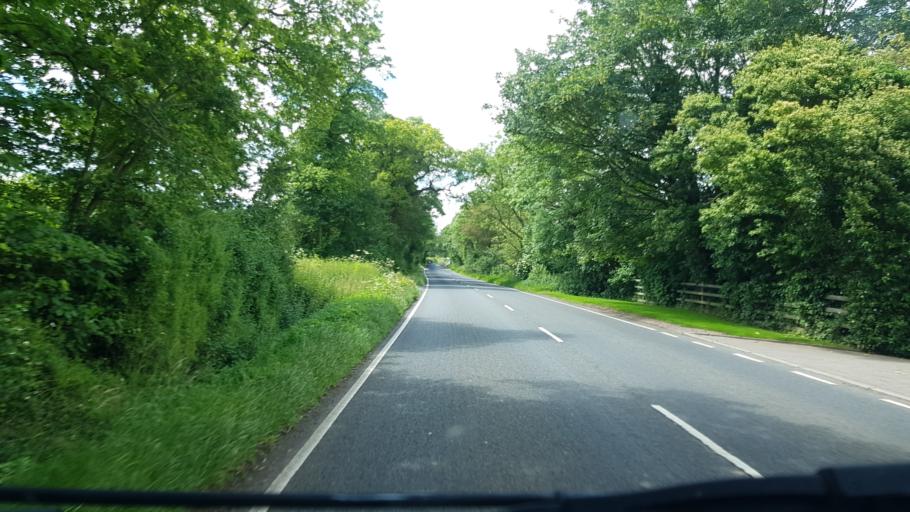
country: GB
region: England
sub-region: Worcestershire
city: Droitwich
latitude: 52.2605
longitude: -2.0771
